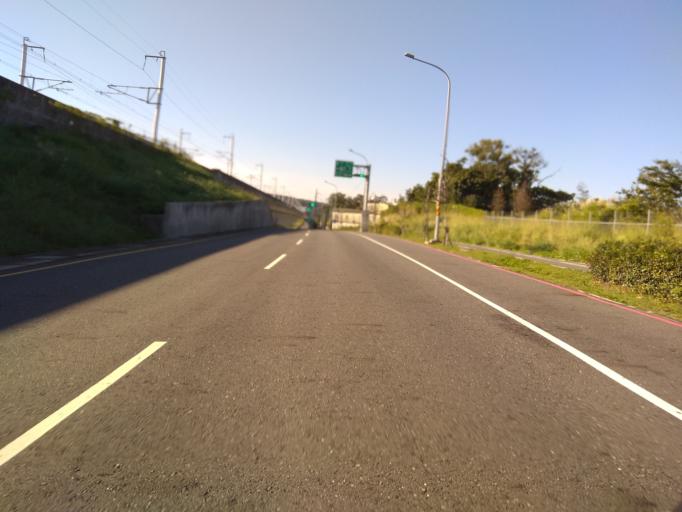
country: TW
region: Taiwan
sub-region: Hsinchu
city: Zhubei
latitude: 24.8921
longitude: 121.0758
